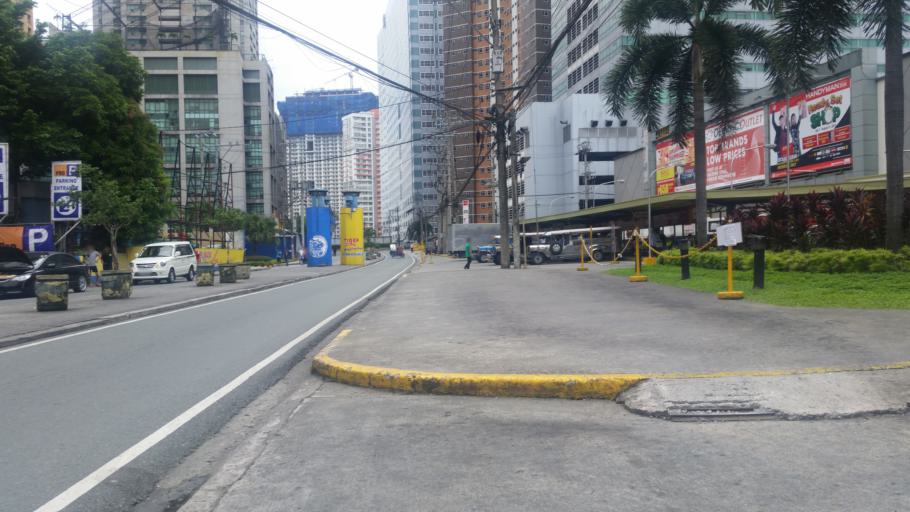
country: PH
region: Metro Manila
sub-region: Mandaluyong
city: Mandaluyong City
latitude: 14.5722
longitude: 121.0477
